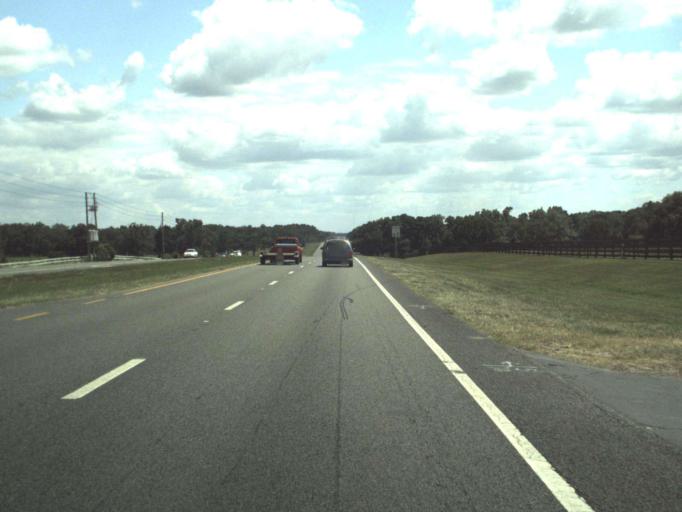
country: US
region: Florida
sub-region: Marion County
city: Ocala
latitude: 29.2887
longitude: -82.1520
